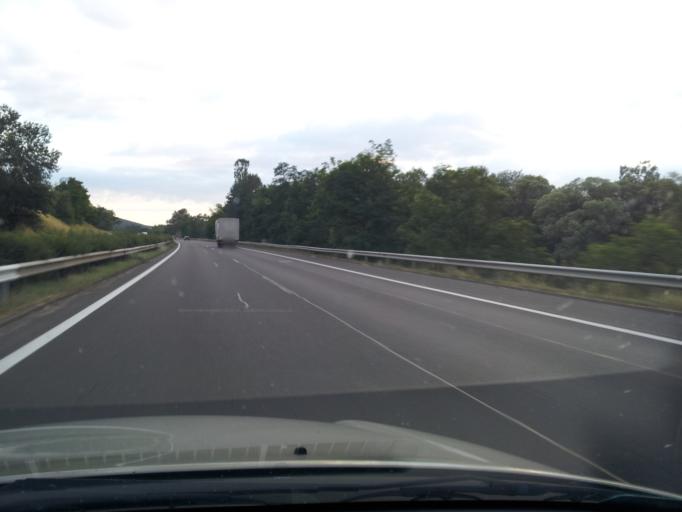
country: HU
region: Pest
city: Bag
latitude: 47.6298
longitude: 19.4526
